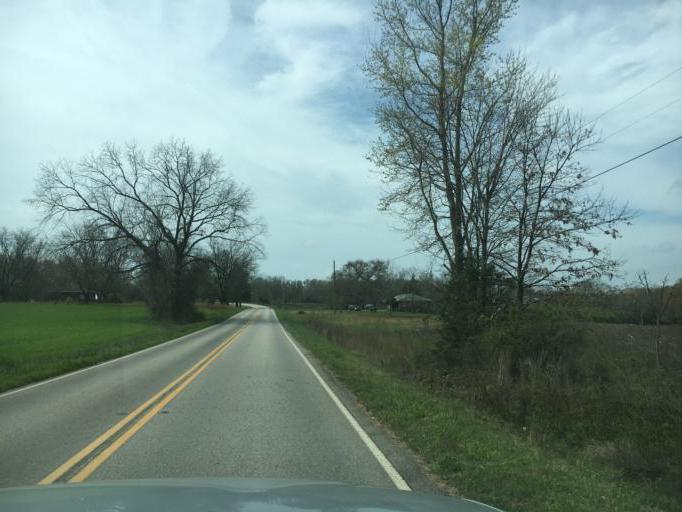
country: US
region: Georgia
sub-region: Hart County
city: Royston
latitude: 34.3239
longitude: -83.0421
